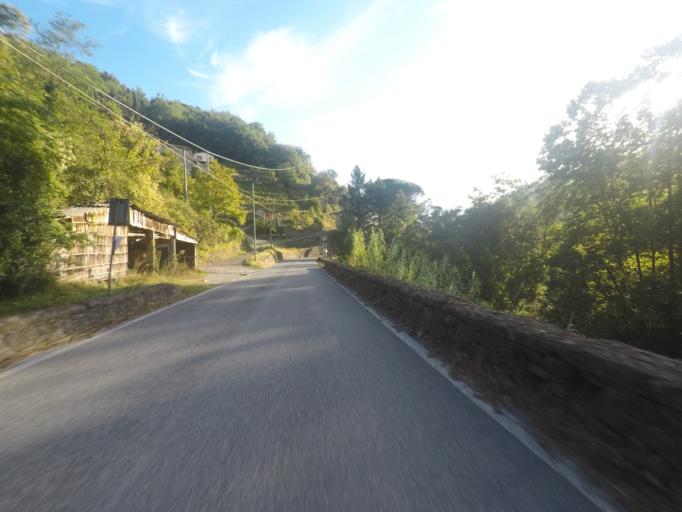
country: IT
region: Tuscany
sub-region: Provincia di Lucca
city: Valdottavo
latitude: 43.9604
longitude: 10.4568
